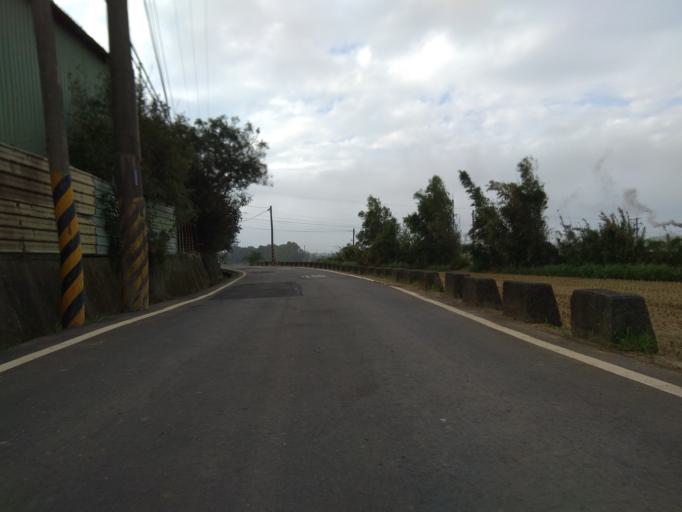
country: TW
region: Taiwan
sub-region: Hsinchu
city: Zhubei
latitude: 24.9743
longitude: 121.0422
